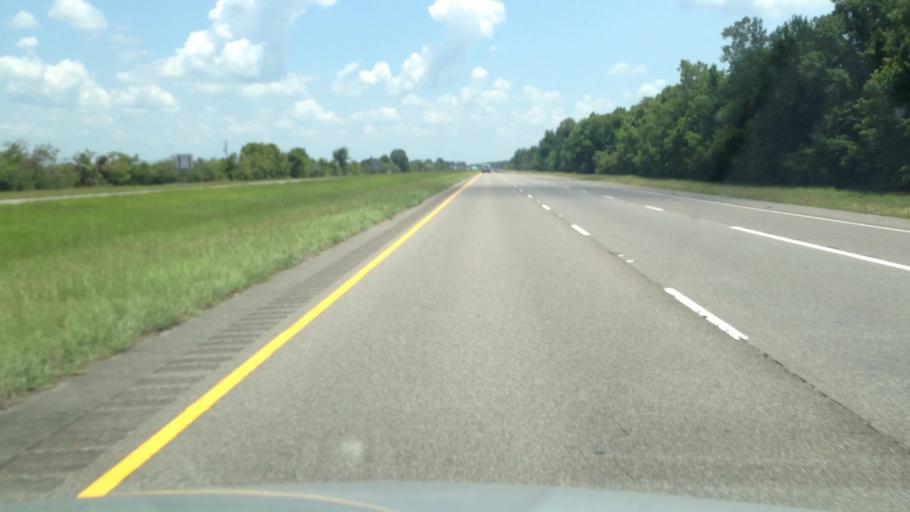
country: US
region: Louisiana
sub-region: Avoyelles Parish
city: Bunkie
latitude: 30.9486
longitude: -92.2734
